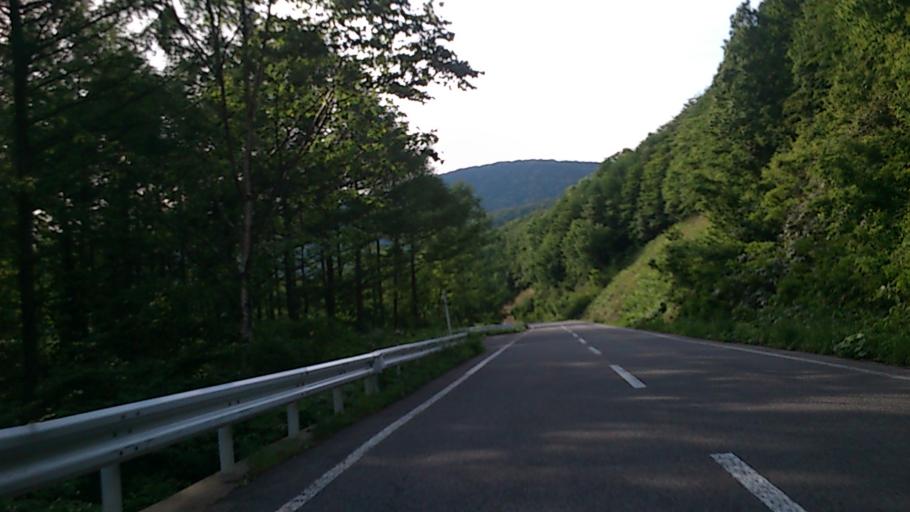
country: JP
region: Aomori
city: Aomori Shi
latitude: 40.6489
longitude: 140.7760
